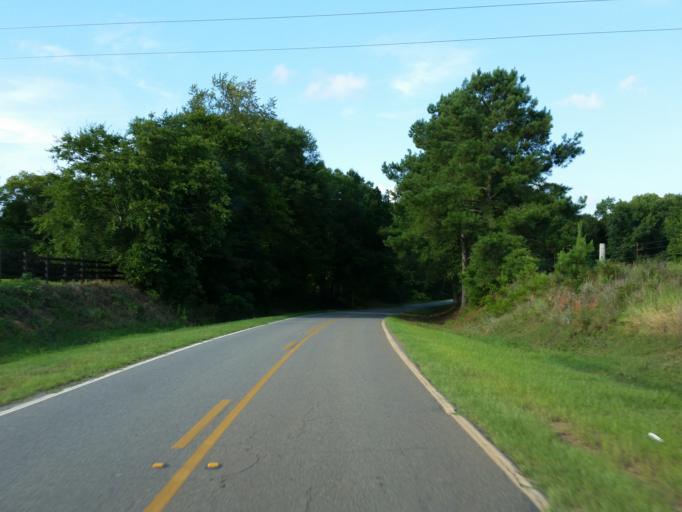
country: US
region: Georgia
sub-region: Lee County
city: Leesburg
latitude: 31.9026
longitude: -84.0416
